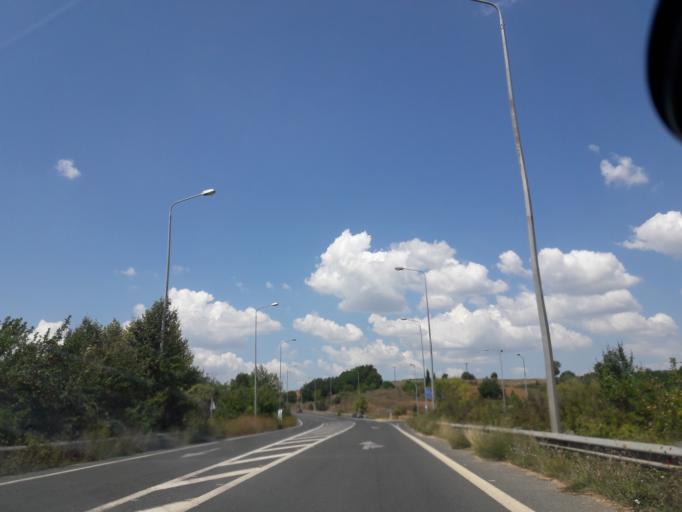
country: GR
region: Central Macedonia
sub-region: Nomos Chalkidikis
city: Galatista
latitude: 40.4643
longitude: 23.3702
